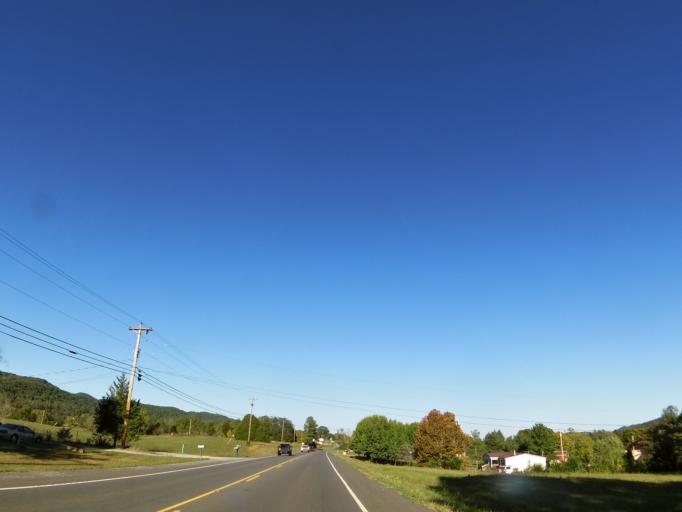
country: US
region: Tennessee
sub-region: Grainger County
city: Rutledge
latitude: 36.2970
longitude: -83.4792
